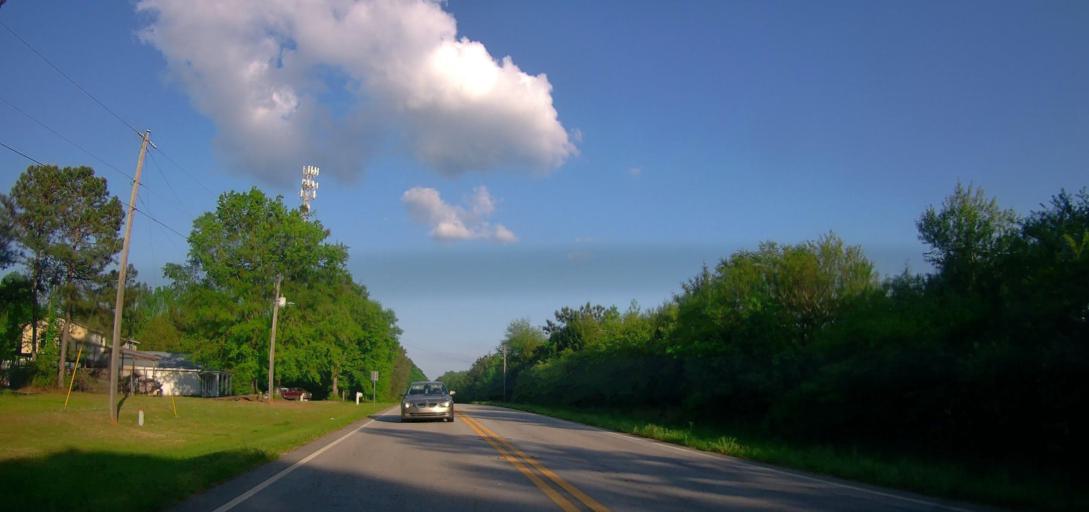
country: US
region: Georgia
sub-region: Jasper County
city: Monticello
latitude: 33.3969
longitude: -83.5826
